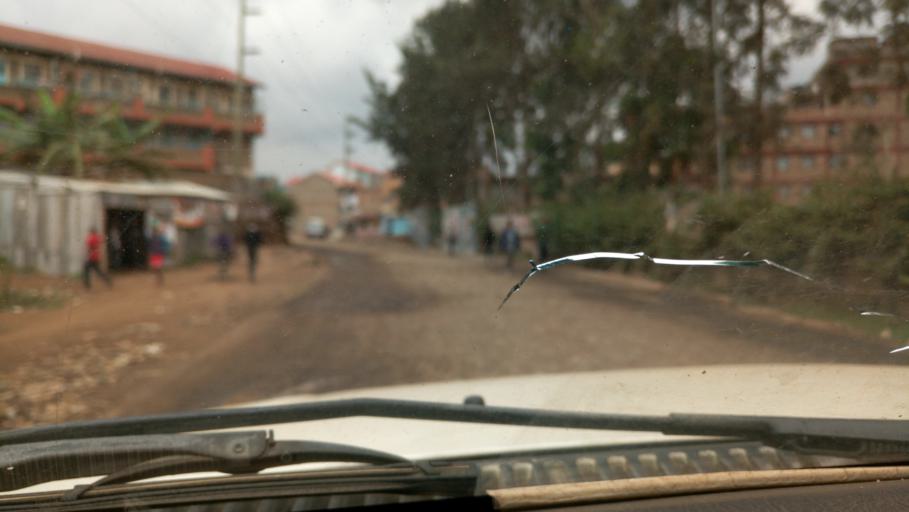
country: KE
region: Nairobi Area
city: Pumwani
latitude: -1.2413
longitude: 36.8942
